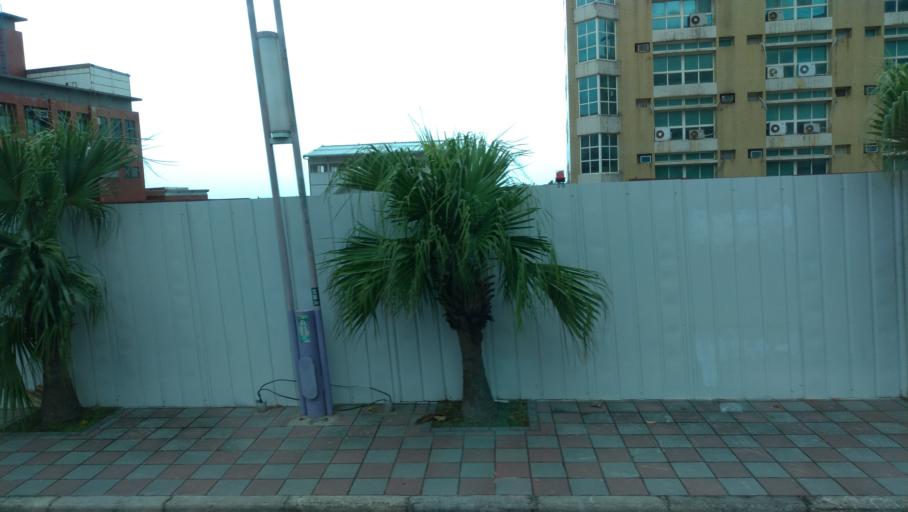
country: TW
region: Taiwan
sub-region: Keelung
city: Keelung
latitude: 25.1507
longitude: 121.7797
